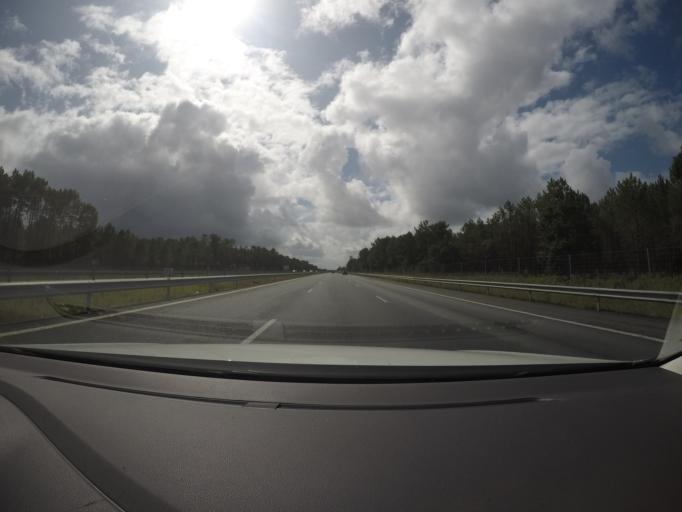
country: FR
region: Aquitaine
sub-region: Departement des Landes
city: Magescq
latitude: 43.7528
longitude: -1.2234
